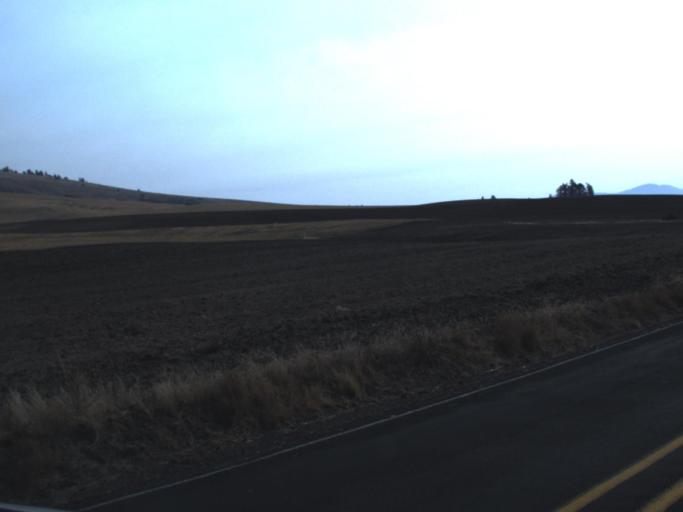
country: US
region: Idaho
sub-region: Benewah County
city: Plummer
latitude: 47.2348
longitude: -117.1173
